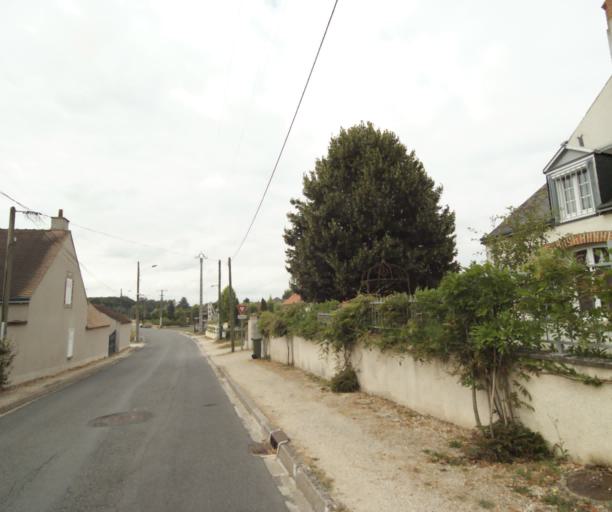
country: FR
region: Centre
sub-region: Departement du Loiret
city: Boigny-sur-Bionne
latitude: 47.9308
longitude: 2.0082
